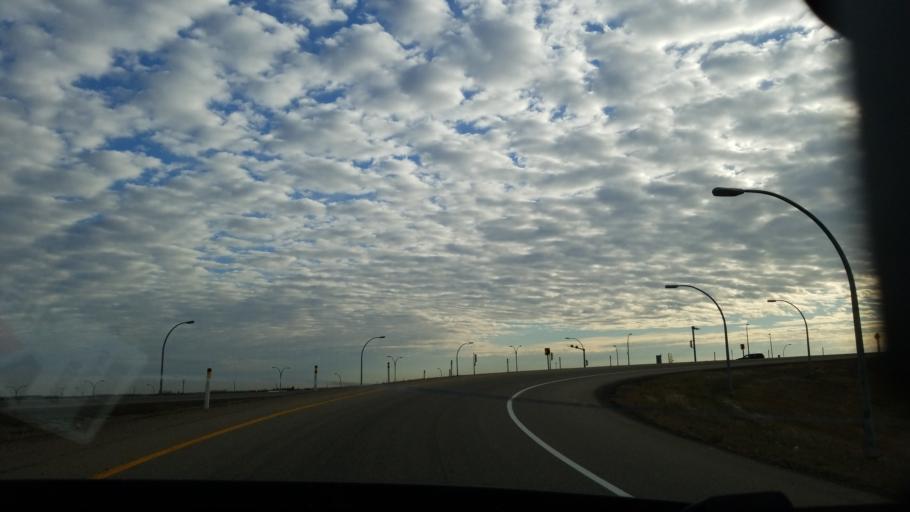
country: CA
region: Alberta
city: Edmonton
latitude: 53.6483
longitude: -113.4400
